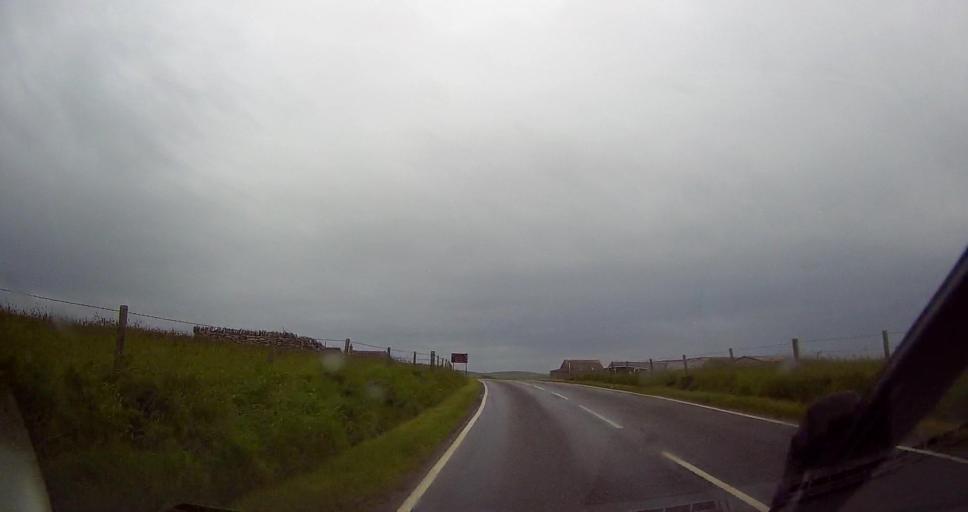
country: GB
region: Scotland
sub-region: Orkney Islands
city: Stromness
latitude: 59.0320
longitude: -3.2866
